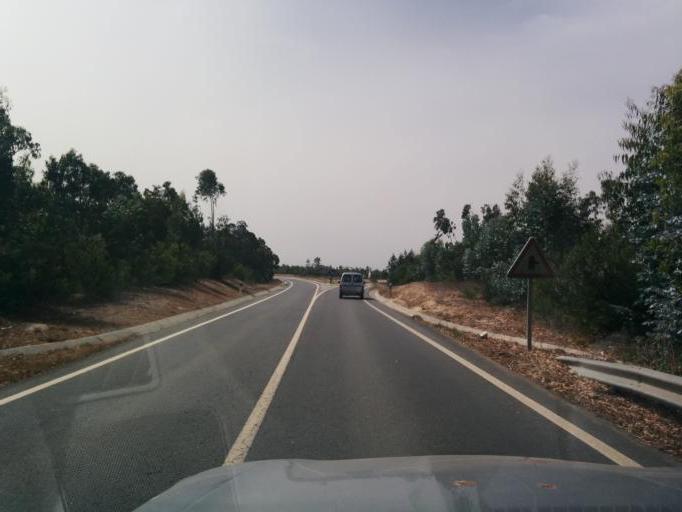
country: PT
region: Beja
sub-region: Odemira
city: Vila Nova de Milfontes
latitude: 37.6442
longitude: -8.7595
